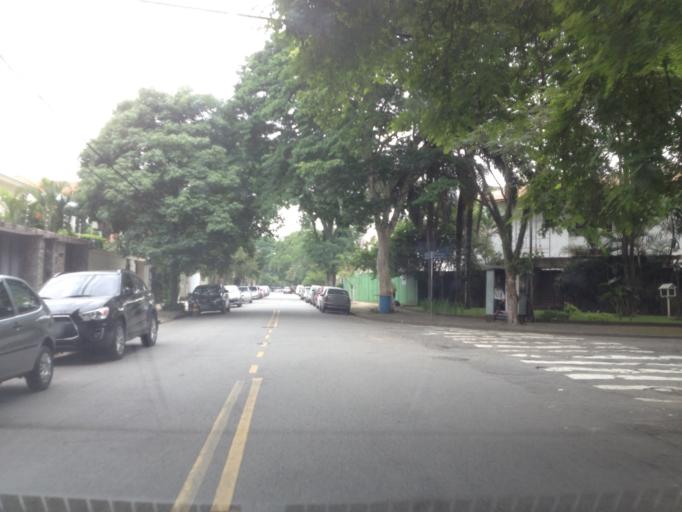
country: BR
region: Sao Paulo
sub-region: Sao Paulo
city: Sao Paulo
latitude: -23.5780
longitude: -46.6615
